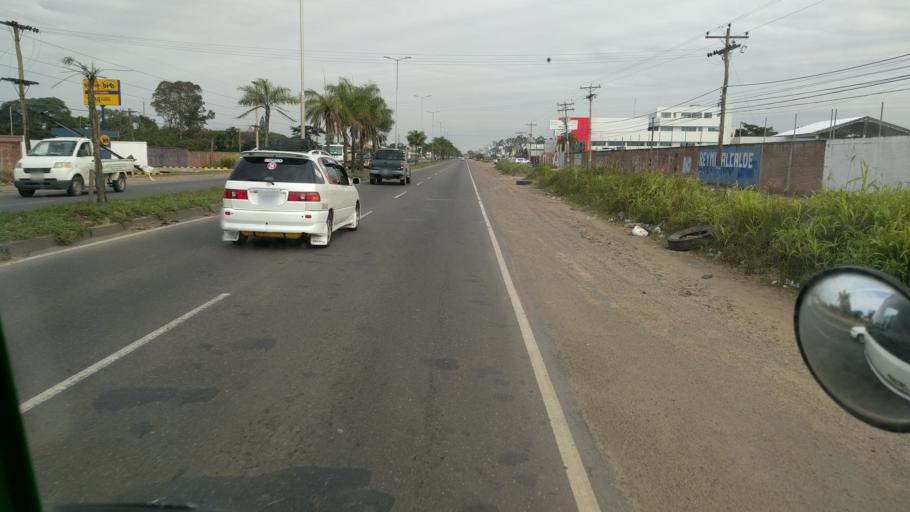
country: BO
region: Santa Cruz
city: Santa Cruz de la Sierra
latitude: -17.6861
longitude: -63.1592
